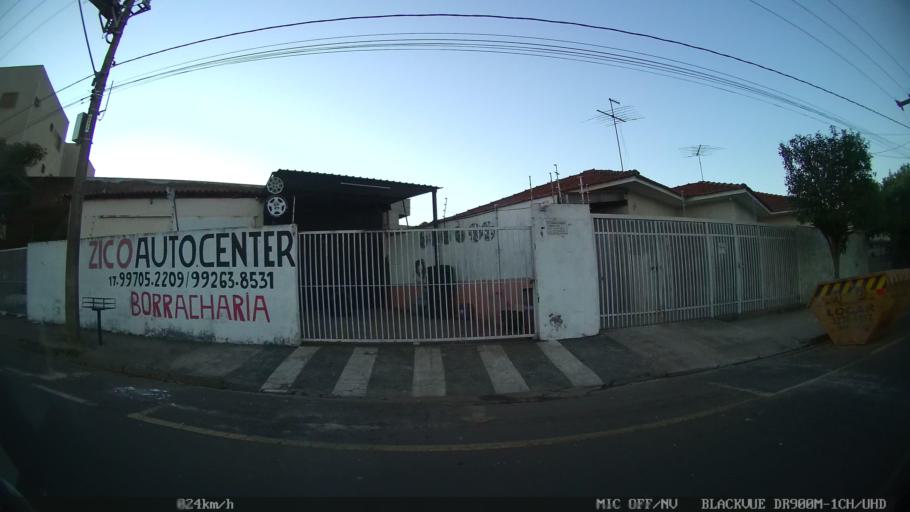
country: BR
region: Sao Paulo
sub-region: Sao Jose Do Rio Preto
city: Sao Jose do Rio Preto
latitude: -20.8421
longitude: -49.3742
